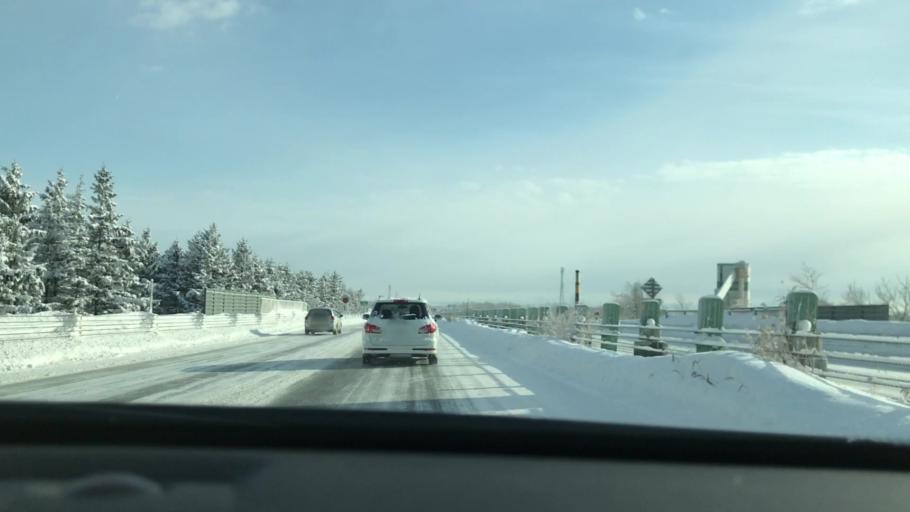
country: JP
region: Hokkaido
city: Sapporo
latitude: 43.0855
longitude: 141.4458
